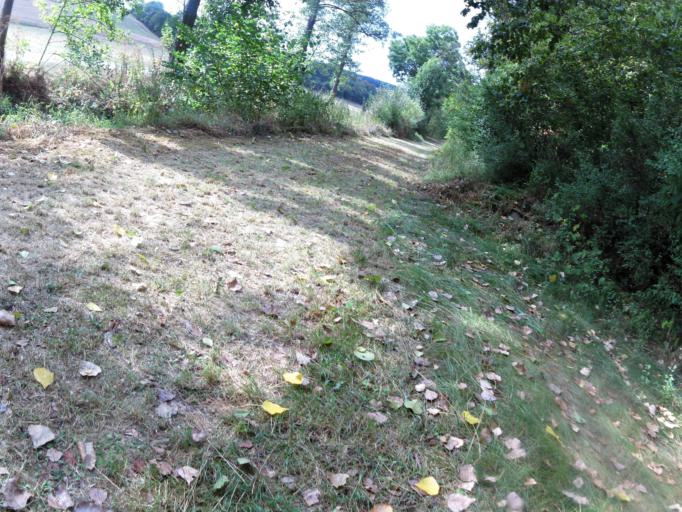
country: DE
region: Bavaria
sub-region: Regierungsbezirk Unterfranken
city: Gadheim
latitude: 49.8503
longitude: 9.9127
